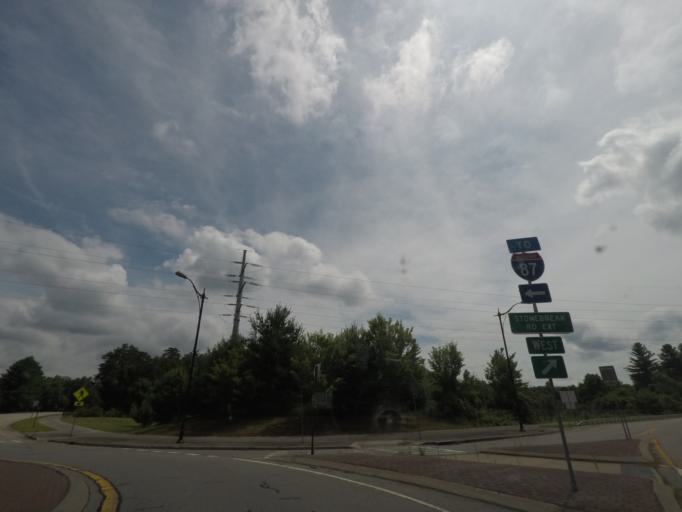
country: US
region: New York
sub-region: Saratoga County
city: Country Knolls
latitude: 42.9633
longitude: -73.7640
